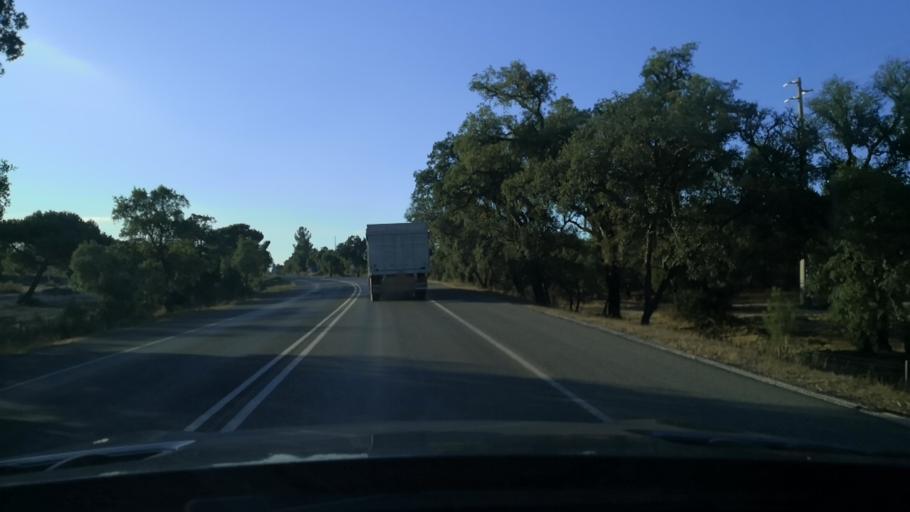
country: PT
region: Evora
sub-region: Vendas Novas
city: Vendas Novas
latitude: 38.5669
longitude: -8.6586
